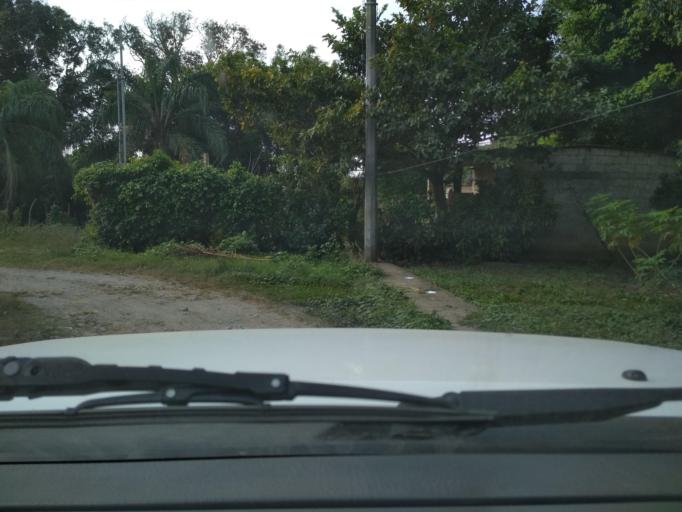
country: MX
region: Veracruz
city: El Tejar
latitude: 19.0814
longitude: -96.1642
